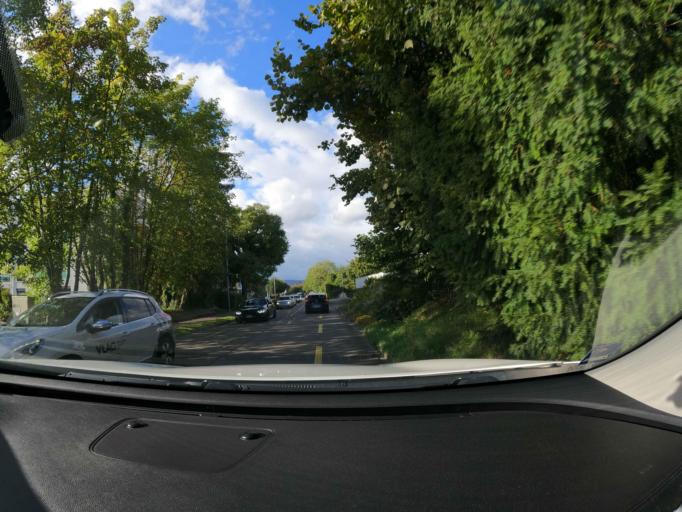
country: CH
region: Aargau
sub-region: Bezirk Brugg
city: Hausen
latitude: 47.4590
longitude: 8.2126
